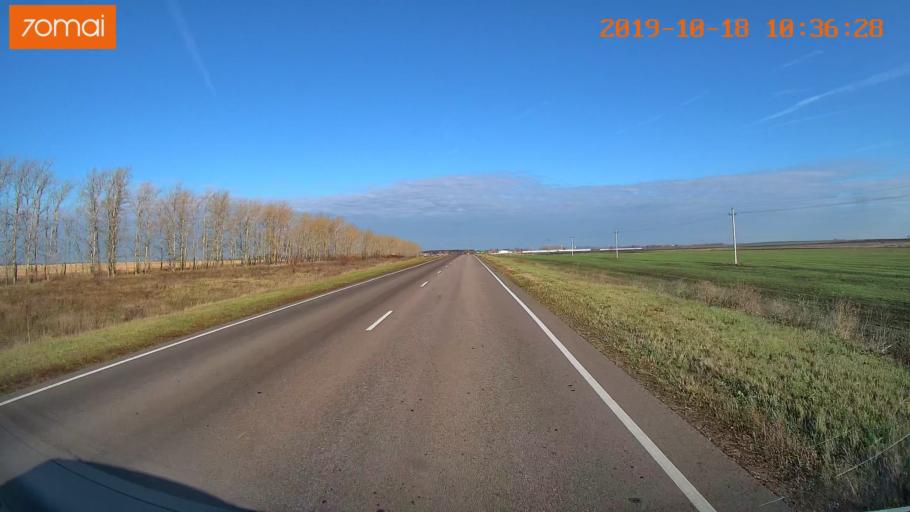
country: RU
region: Tula
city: Kurkino
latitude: 53.5486
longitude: 38.6258
